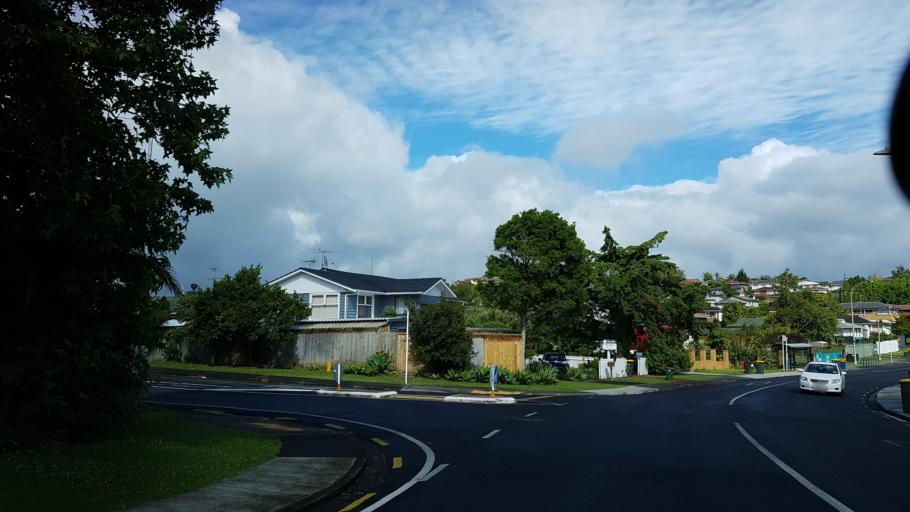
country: NZ
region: Auckland
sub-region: Auckland
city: North Shore
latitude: -36.7966
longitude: 174.7370
